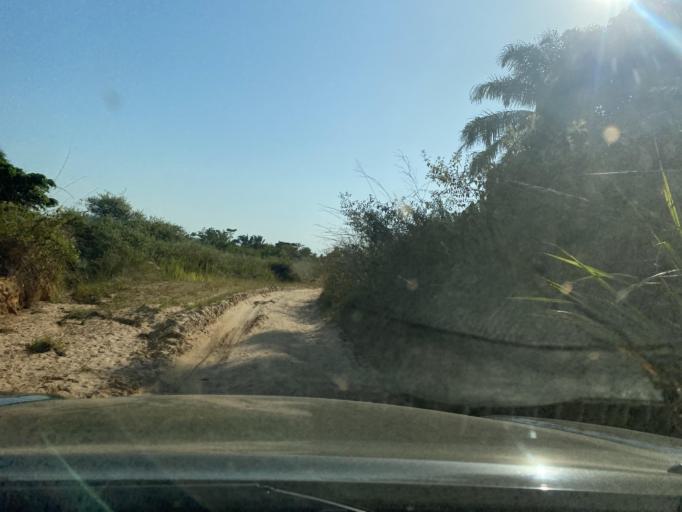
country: CD
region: Kasai-Oriental
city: Kabinda
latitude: -6.1166
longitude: 24.3566
